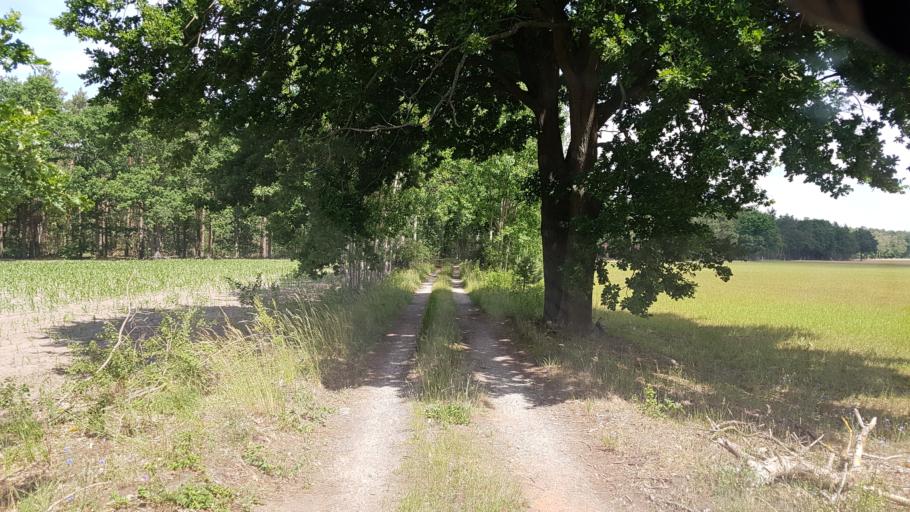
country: DE
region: Brandenburg
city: Ruckersdorf
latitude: 51.6035
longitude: 13.6246
